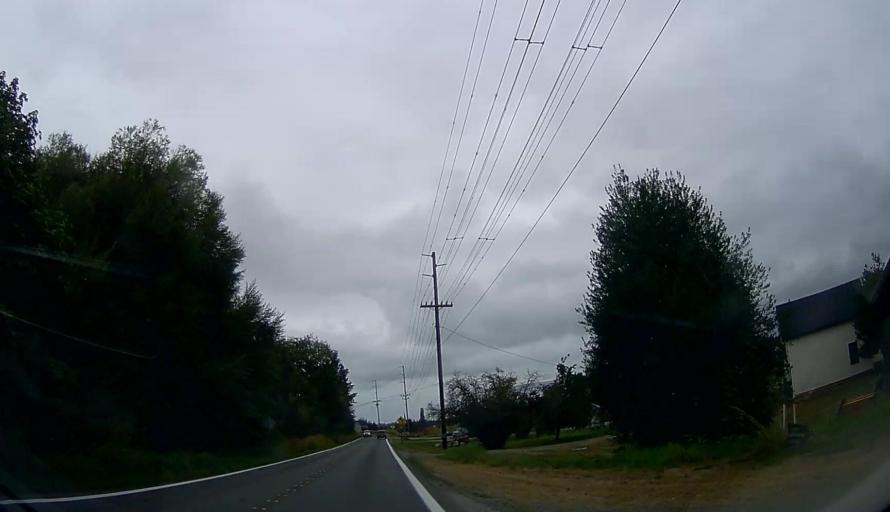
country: US
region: Washington
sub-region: Snohomish County
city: Stanwood
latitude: 48.2265
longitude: -122.3388
